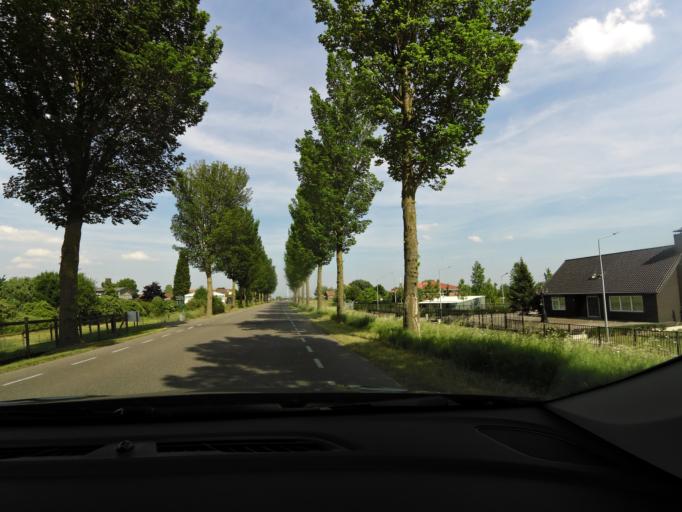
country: NL
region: South Holland
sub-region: Gemeente Spijkenisse
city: Spijkenisse
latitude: 51.7909
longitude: 4.3101
